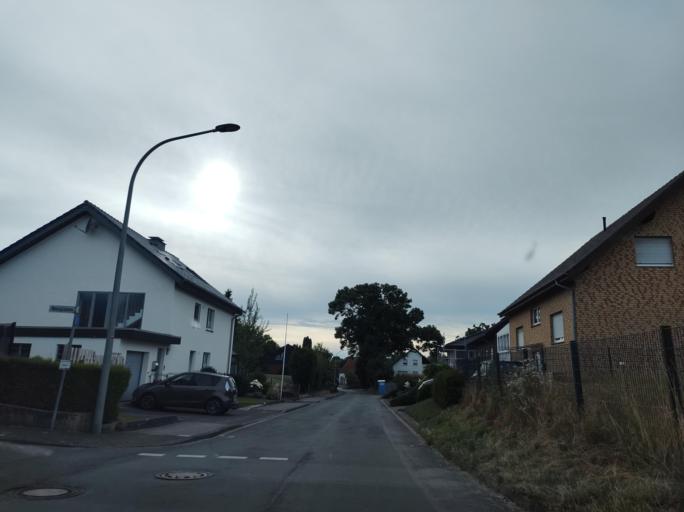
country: DE
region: North Rhine-Westphalia
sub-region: Regierungsbezirk Detmold
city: Salzkotten
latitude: 51.6530
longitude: 8.6053
